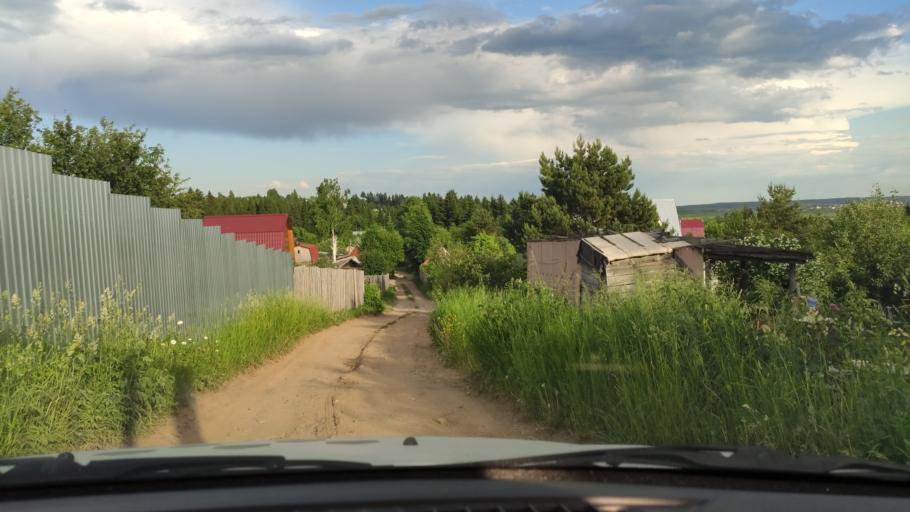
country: RU
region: Perm
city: Kondratovo
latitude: 57.9437
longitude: 56.1829
